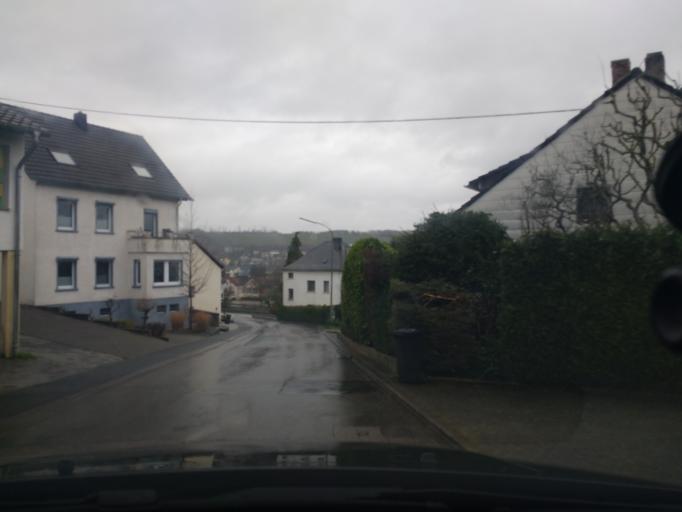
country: LU
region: Grevenmacher
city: Wasserbillig
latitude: 49.7094
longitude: 6.5069
